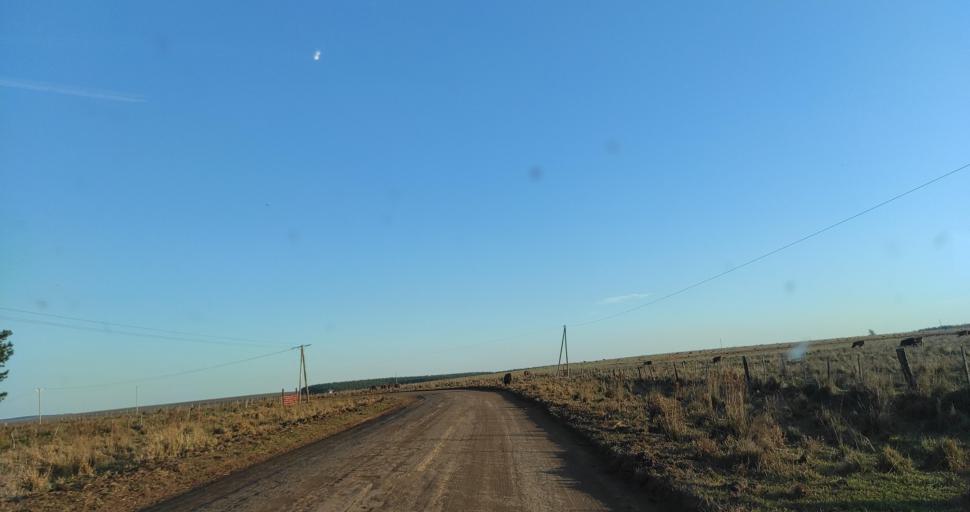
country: PY
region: Itapua
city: San Juan del Parana
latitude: -27.4329
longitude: -56.0849
